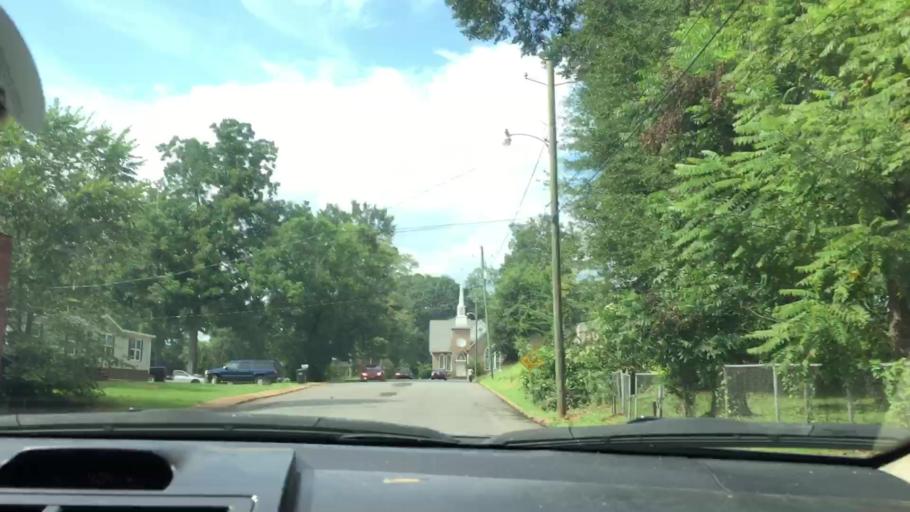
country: US
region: Alabama
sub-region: Hale County
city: Greensboro
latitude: 32.7059
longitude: -87.5893
